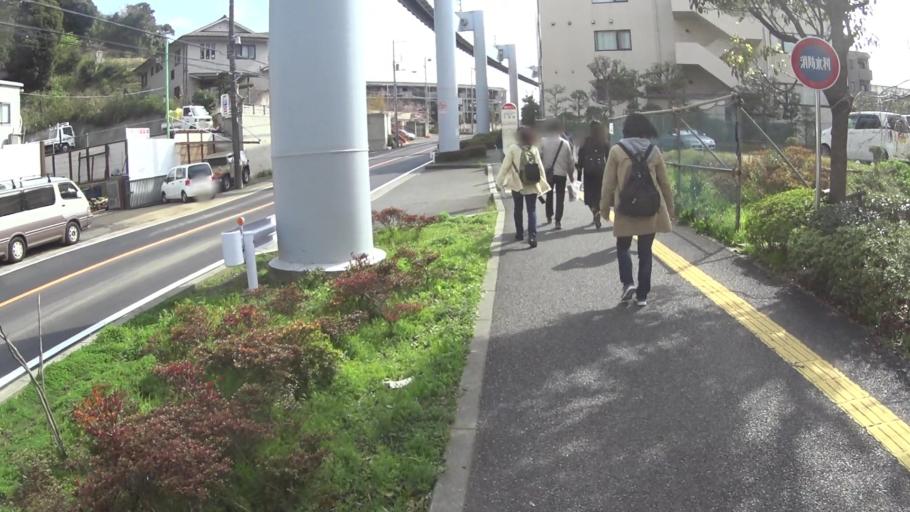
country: JP
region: Kanagawa
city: Kamakura
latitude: 35.3367
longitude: 139.5224
